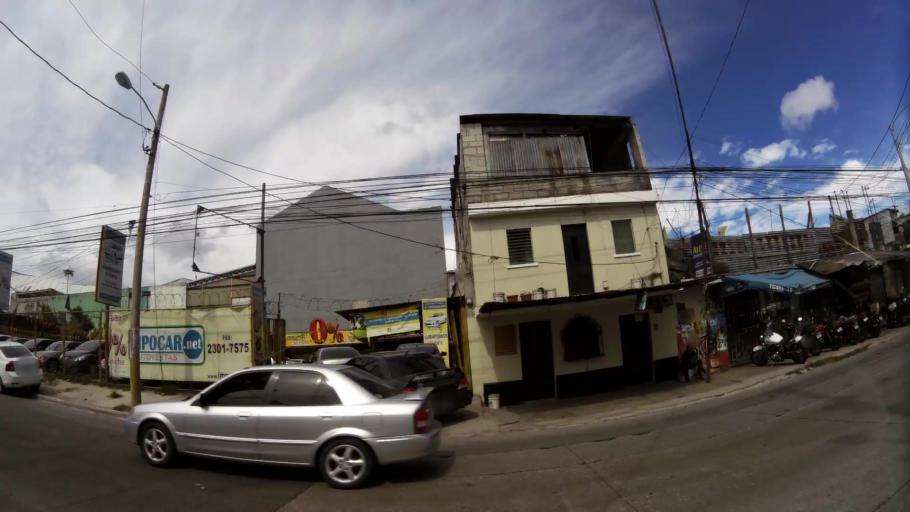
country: GT
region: Guatemala
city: Mixco
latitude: 14.6371
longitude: -90.5797
